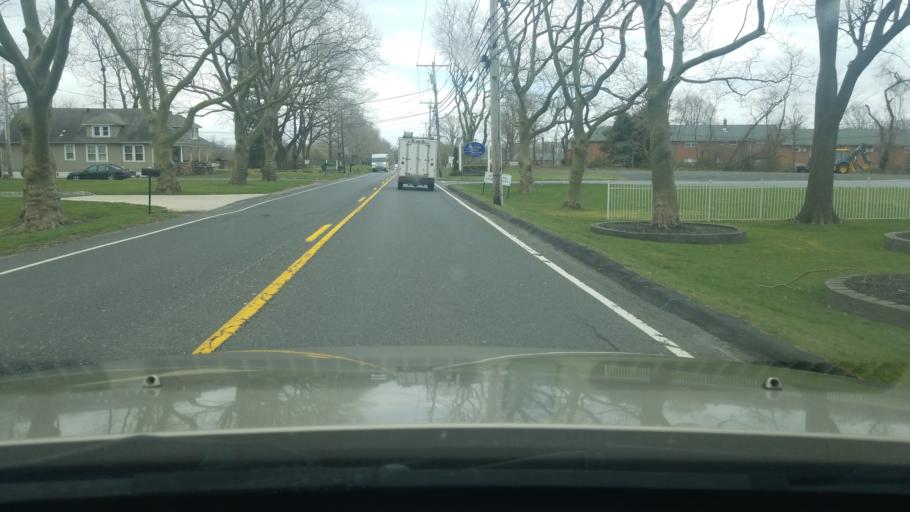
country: US
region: New Jersey
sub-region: Monmouth County
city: Manasquan
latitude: 40.1342
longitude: -74.0727
